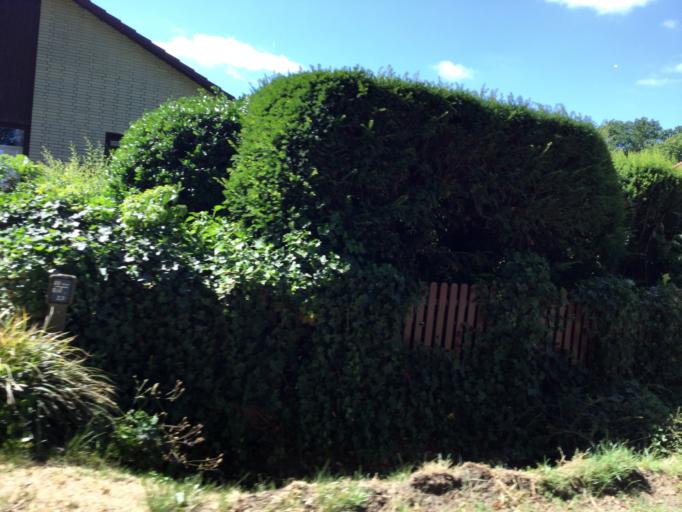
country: DE
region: Hamburg
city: Sasel
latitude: 53.6378
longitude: 10.1402
